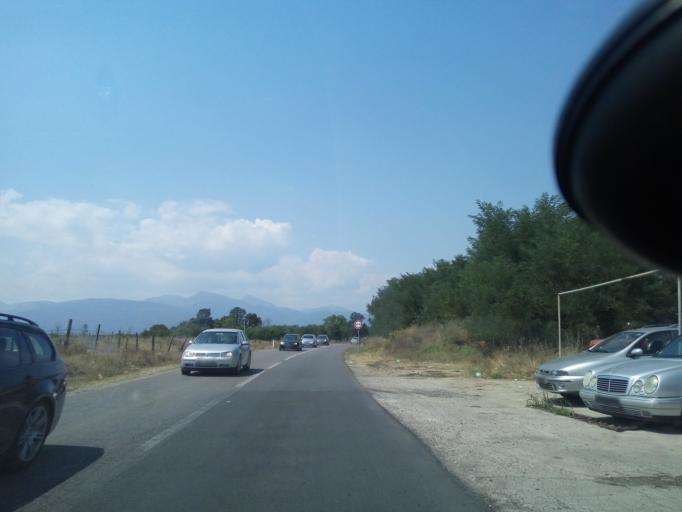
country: XK
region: Gjakova
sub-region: Komuna e Decanit
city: Gllogjan
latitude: 42.4372
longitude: 20.3713
